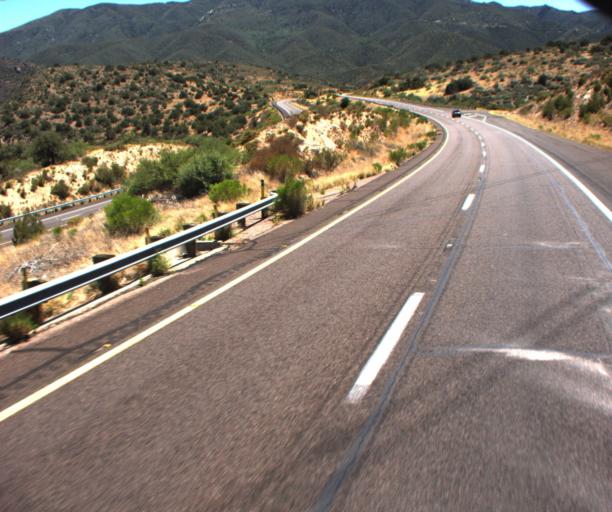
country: US
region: Arizona
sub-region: Gila County
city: Tonto Basin
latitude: 33.9703
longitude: -111.3873
